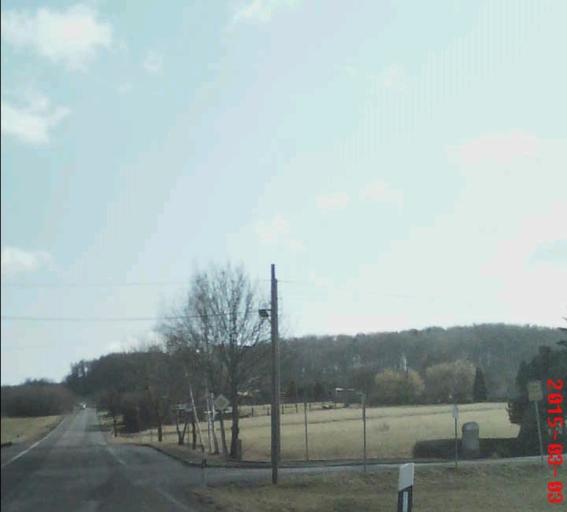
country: DE
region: Thuringia
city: Gosswitz
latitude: 50.6404
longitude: 11.4740
